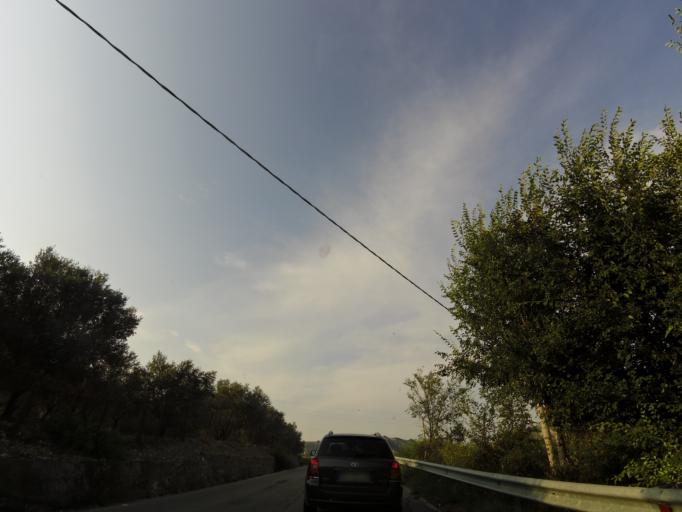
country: IT
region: Calabria
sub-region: Provincia di Reggio Calabria
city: Stilo
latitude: 38.4719
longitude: 16.4768
